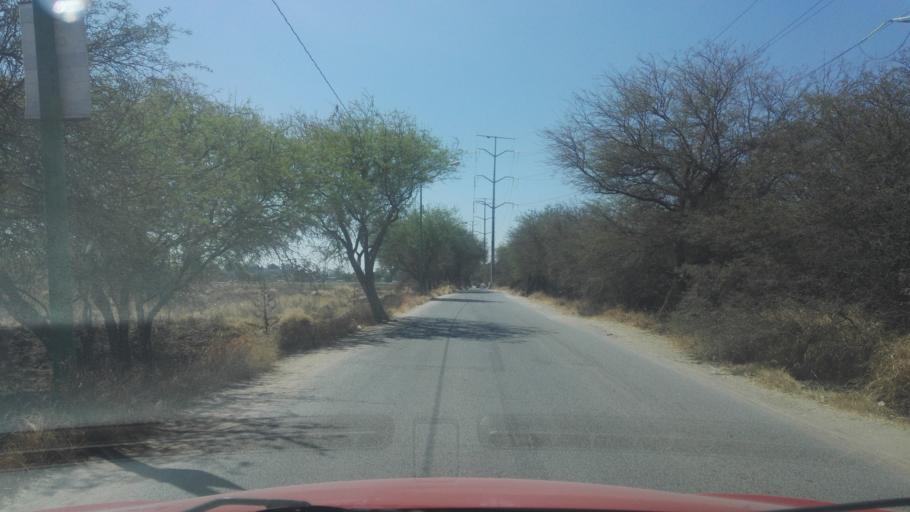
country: MX
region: Guanajuato
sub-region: Leon
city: Fraccionamiento Paraiso Real
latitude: 21.0779
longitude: -101.5981
